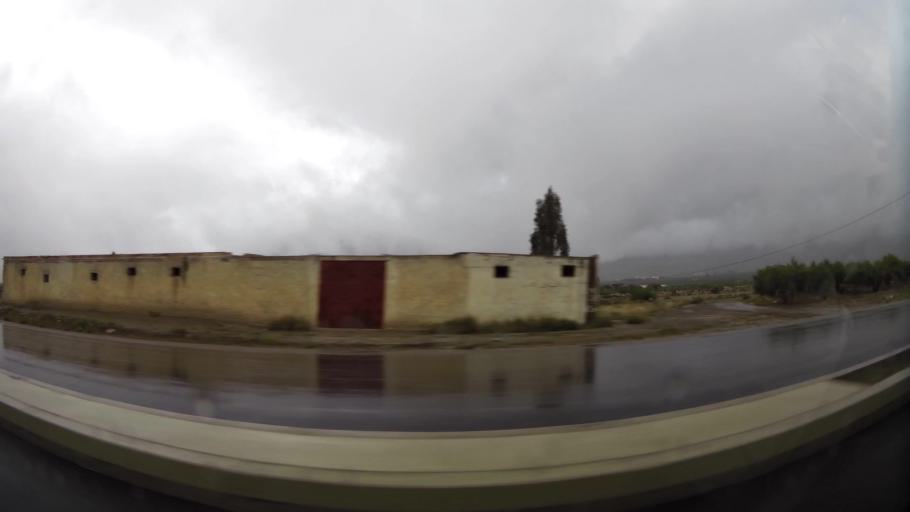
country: MA
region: Oriental
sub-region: Nador
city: Midar
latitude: 34.8319
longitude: -3.7197
